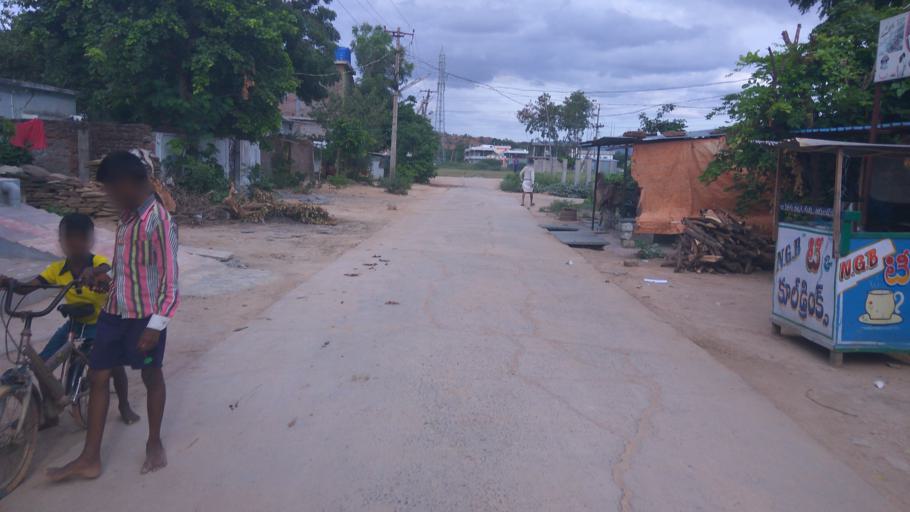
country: IN
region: Andhra Pradesh
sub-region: Prakasam
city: Cumbum
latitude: 15.5903
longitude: 79.1106
